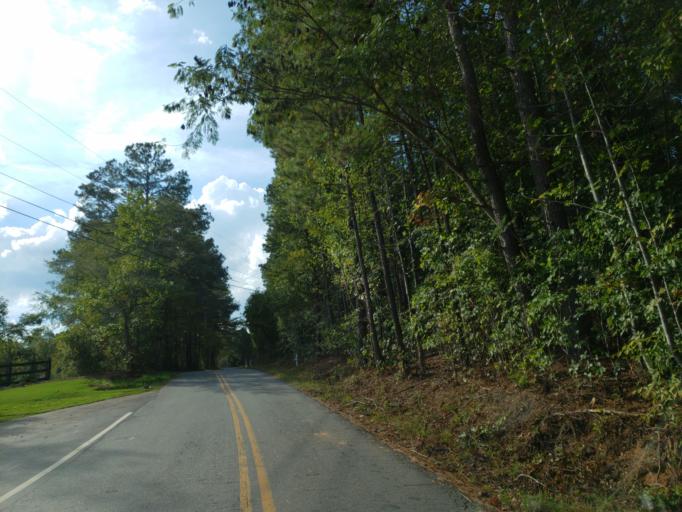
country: US
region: Georgia
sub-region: Fulton County
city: Roswell
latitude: 34.0848
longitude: -84.4197
